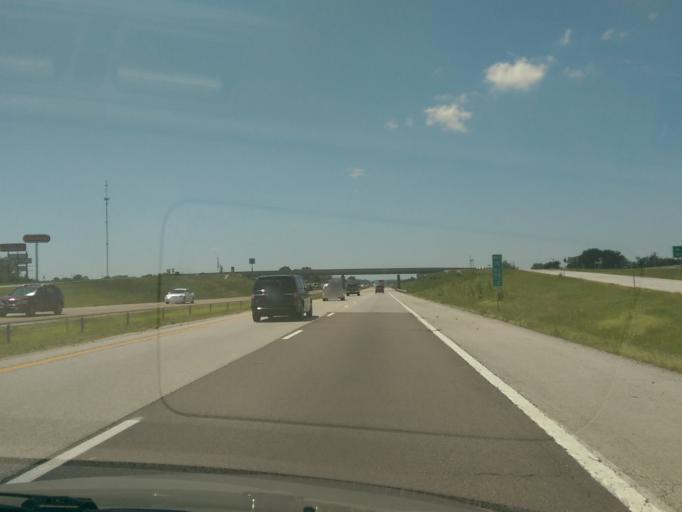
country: US
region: Missouri
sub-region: Cooper County
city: Boonville
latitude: 38.9353
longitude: -92.8444
